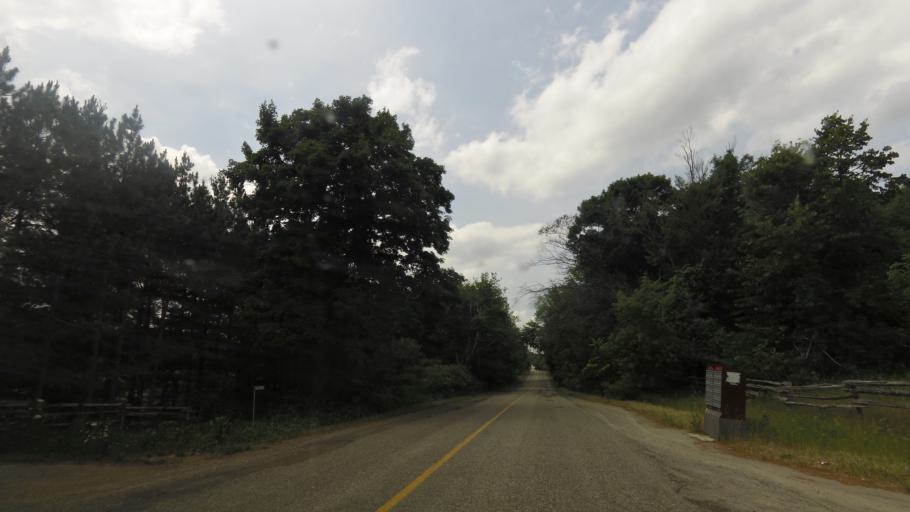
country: CA
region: Ontario
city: Orangeville
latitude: 43.8610
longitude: -79.9012
